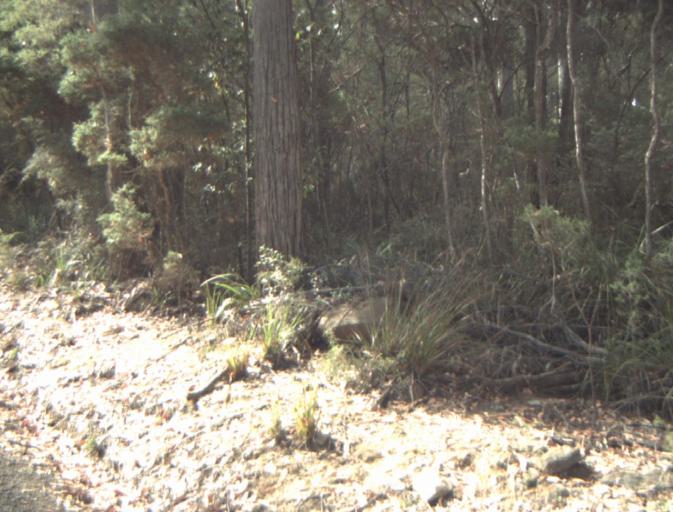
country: AU
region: Tasmania
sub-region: Launceston
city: Mayfield
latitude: -41.2651
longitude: 147.2329
